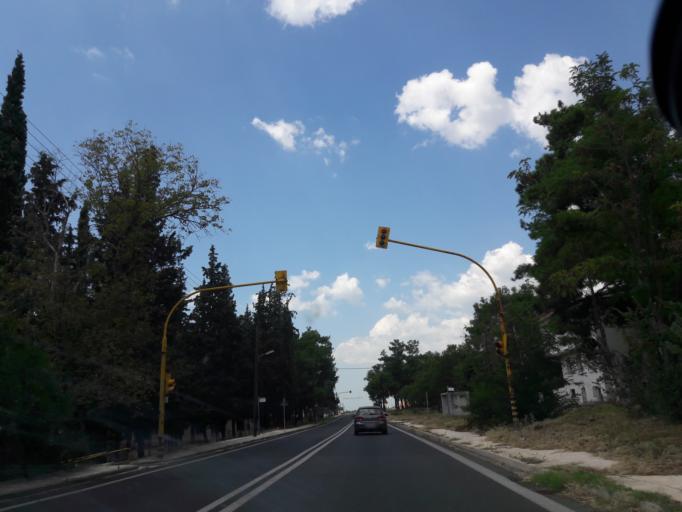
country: GR
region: Central Macedonia
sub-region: Nomos Thessalonikis
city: Agia Paraskevi
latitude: 40.5130
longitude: 23.0763
